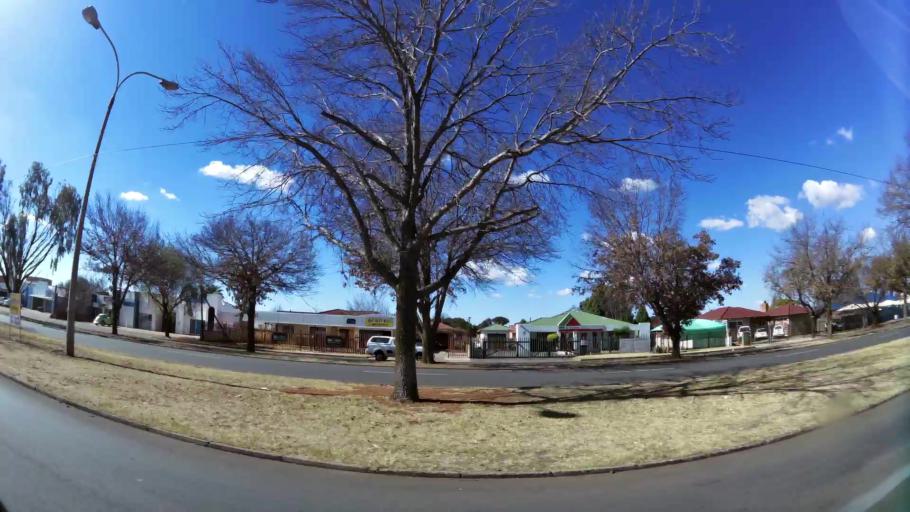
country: ZA
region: Gauteng
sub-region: West Rand District Municipality
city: Carletonville
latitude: -26.3589
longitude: 27.4007
